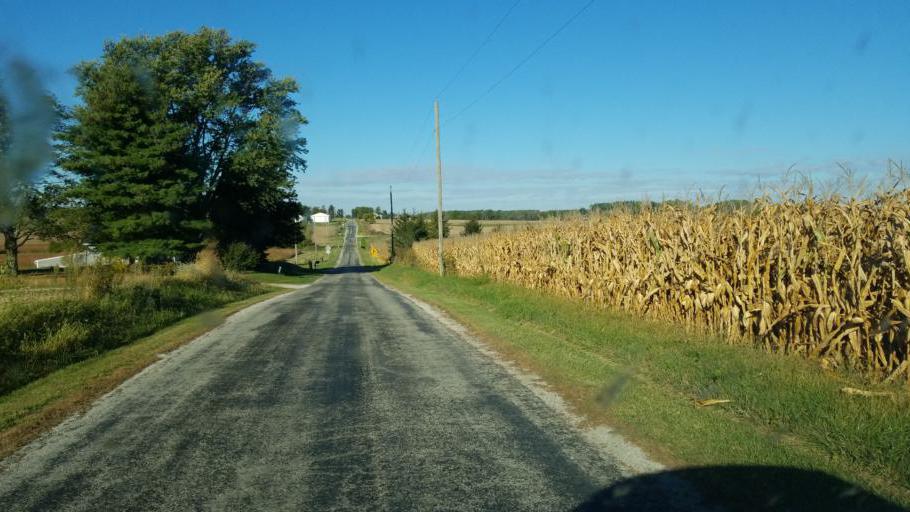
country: US
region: Ohio
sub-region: Crawford County
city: Galion
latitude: 40.6977
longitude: -82.8612
